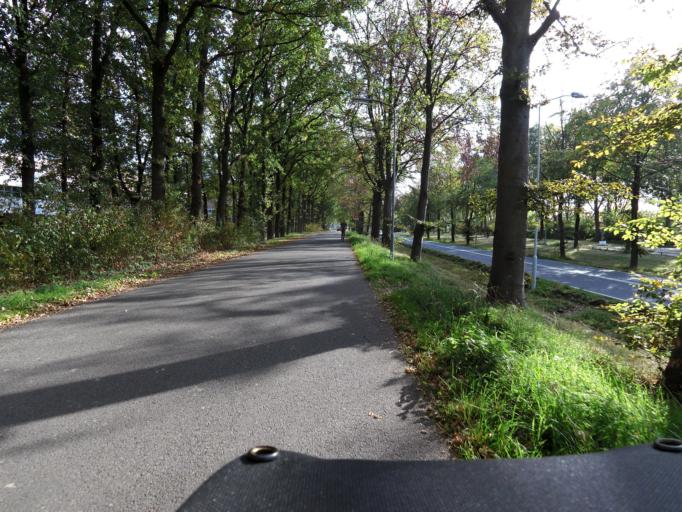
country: NL
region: Gelderland
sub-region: Gemeente Wageningen
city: Wageningen
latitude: 51.9719
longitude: 5.6536
